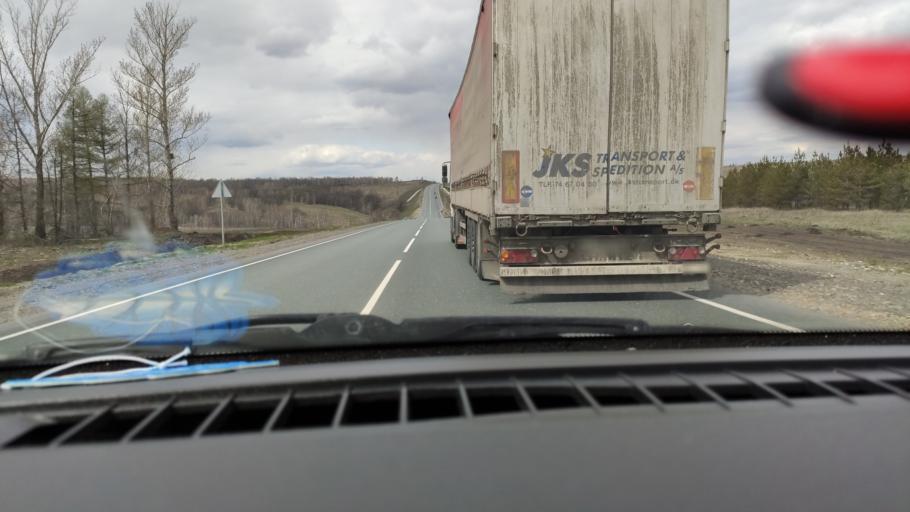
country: RU
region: Saratov
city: Shikhany
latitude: 52.1402
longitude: 47.2091
